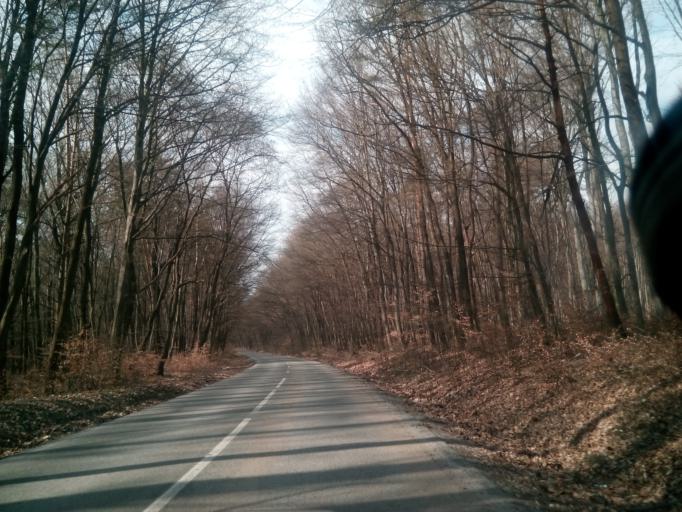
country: SK
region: Kosicky
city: Kosice
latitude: 48.7078
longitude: 21.3802
